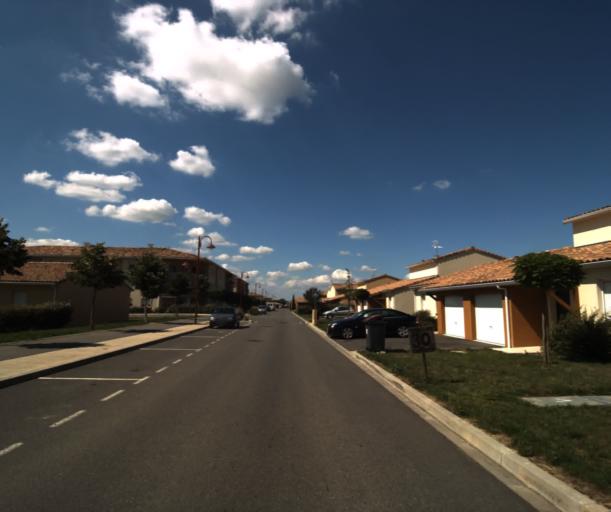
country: FR
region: Midi-Pyrenees
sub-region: Departement de la Haute-Garonne
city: Saint-Lys
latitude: 43.5208
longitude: 1.1888
